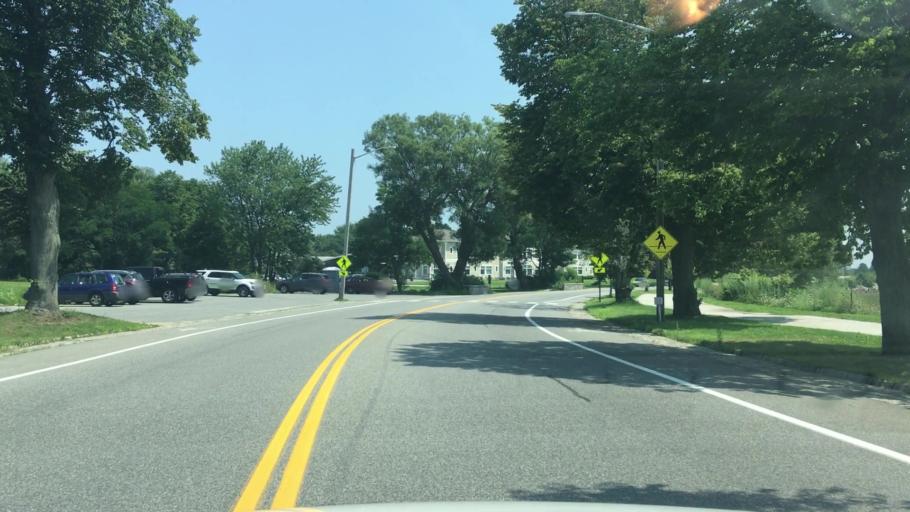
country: US
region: Maine
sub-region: Cumberland County
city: Portland
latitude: 43.6794
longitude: -70.2653
